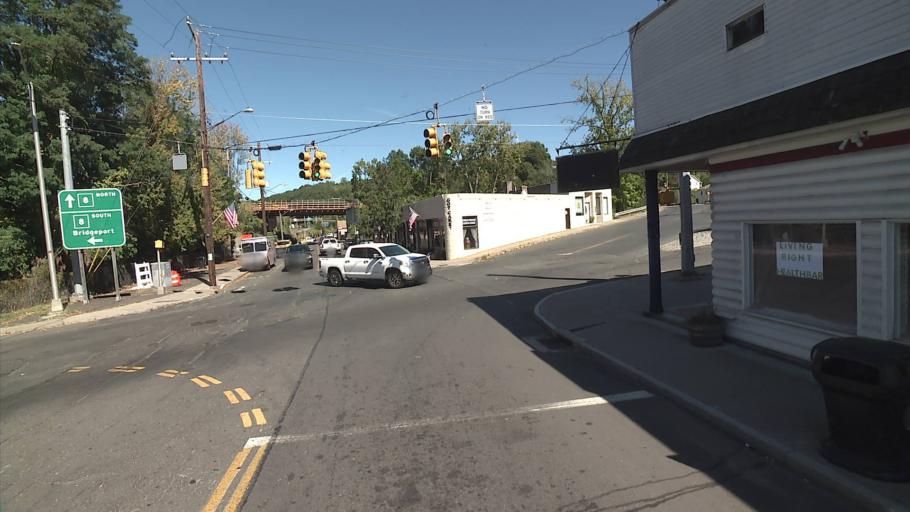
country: US
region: Connecticut
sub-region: New Haven County
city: Naugatuck
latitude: 41.5013
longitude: -73.0472
